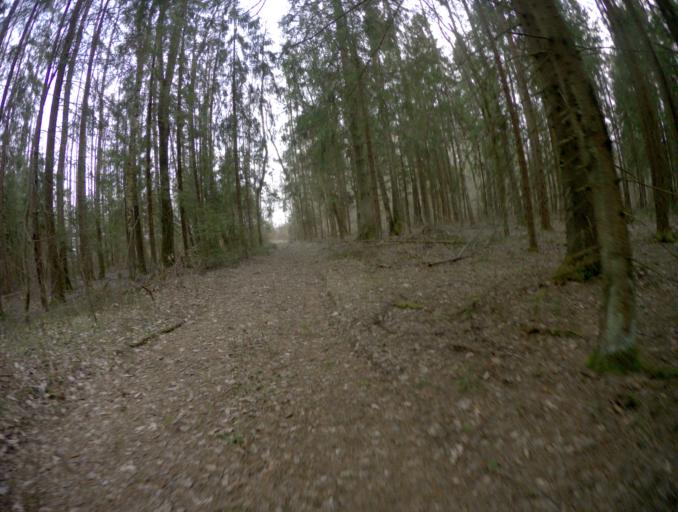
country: RU
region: Vladimir
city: Kommunar
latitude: 56.0784
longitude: 40.5266
